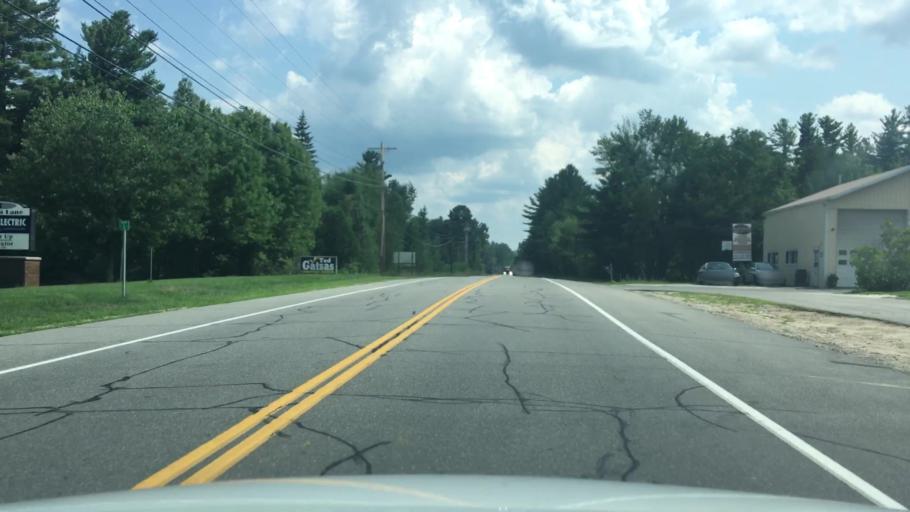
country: US
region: New Hampshire
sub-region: Rockingham County
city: Auburn
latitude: 42.9530
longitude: -71.3539
